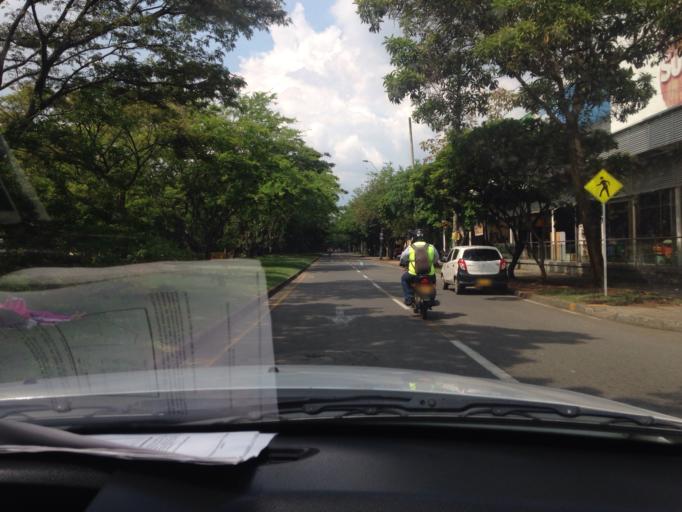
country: CO
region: Valle del Cauca
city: Cali
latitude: 3.3820
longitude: -76.5162
